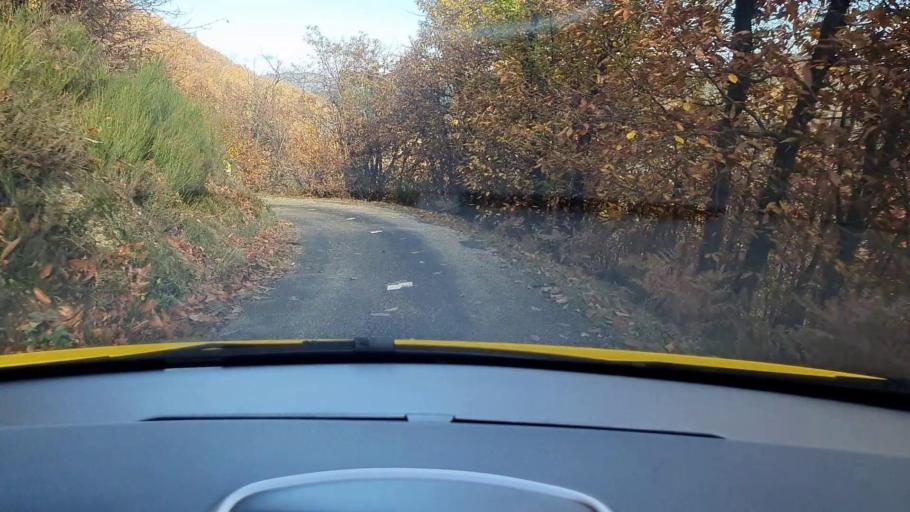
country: FR
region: Languedoc-Roussillon
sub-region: Departement du Gard
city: Valleraugue
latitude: 44.0897
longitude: 3.7434
